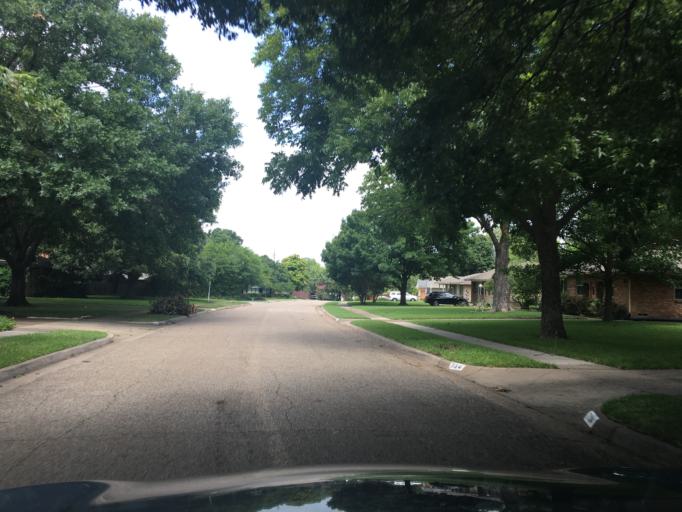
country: US
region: Texas
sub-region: Dallas County
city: Richardson
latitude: 32.9454
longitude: -96.7476
